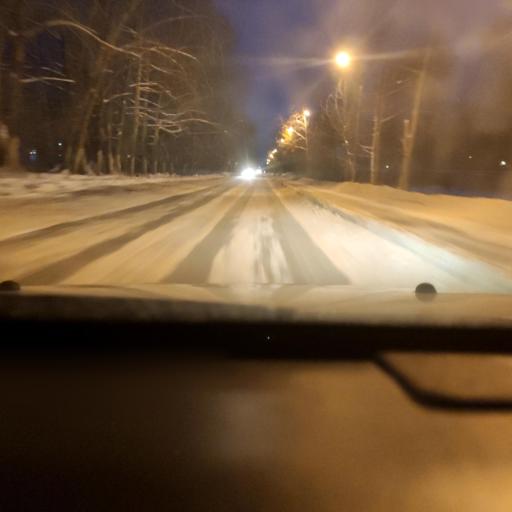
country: RU
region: Perm
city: Perm
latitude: 58.1172
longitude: 56.2903
